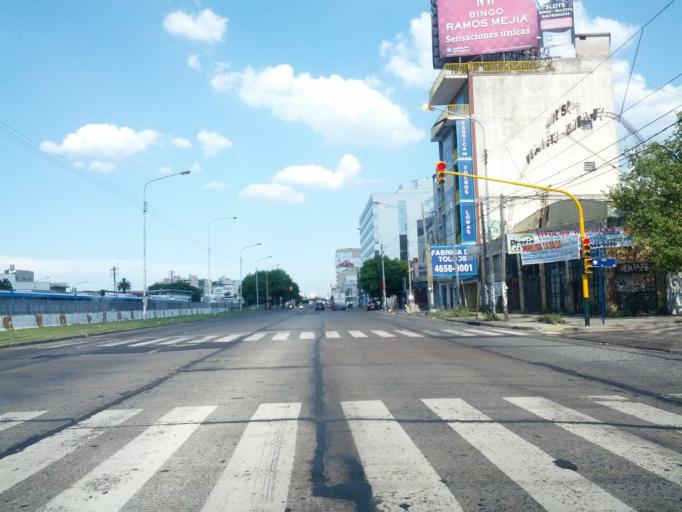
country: AR
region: Buenos Aires
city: San Justo
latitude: -34.6399
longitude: -58.5560
